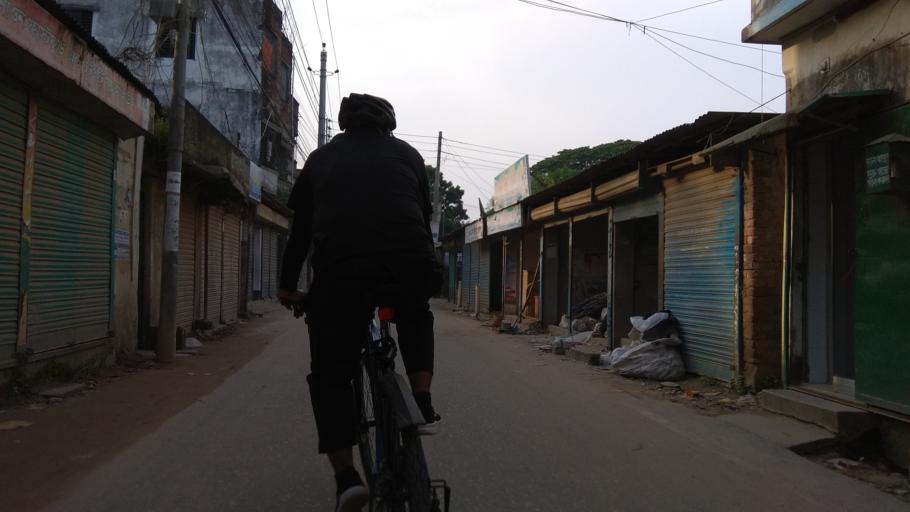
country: BD
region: Dhaka
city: Tungi
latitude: 23.8350
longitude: 90.3879
